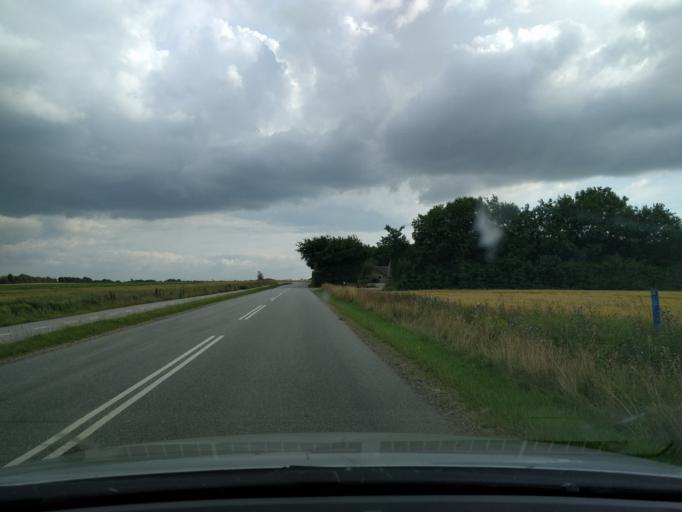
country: DK
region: Central Jutland
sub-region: Herning Kommune
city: Snejbjerg
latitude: 56.1243
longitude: 8.9069
